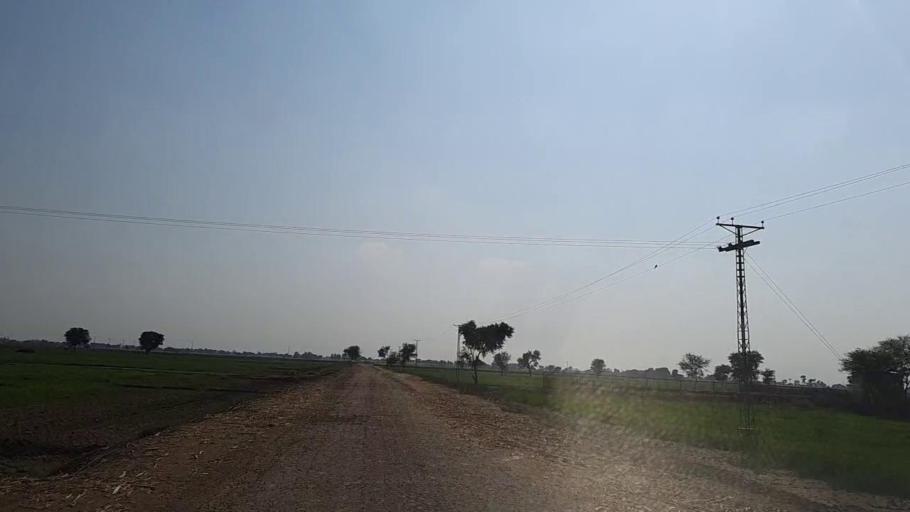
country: PK
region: Sindh
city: Daur
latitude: 26.4473
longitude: 68.2346
